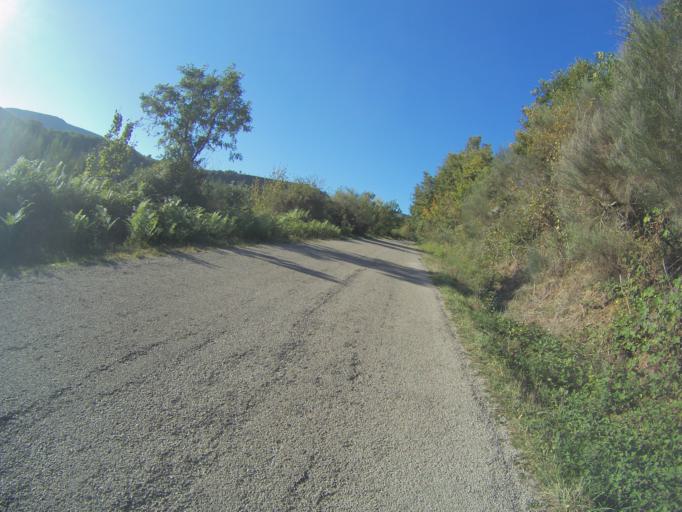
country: ES
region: Castille and Leon
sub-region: Provincia de Leon
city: Vega de Valcarce
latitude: 42.6875
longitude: -7.0062
